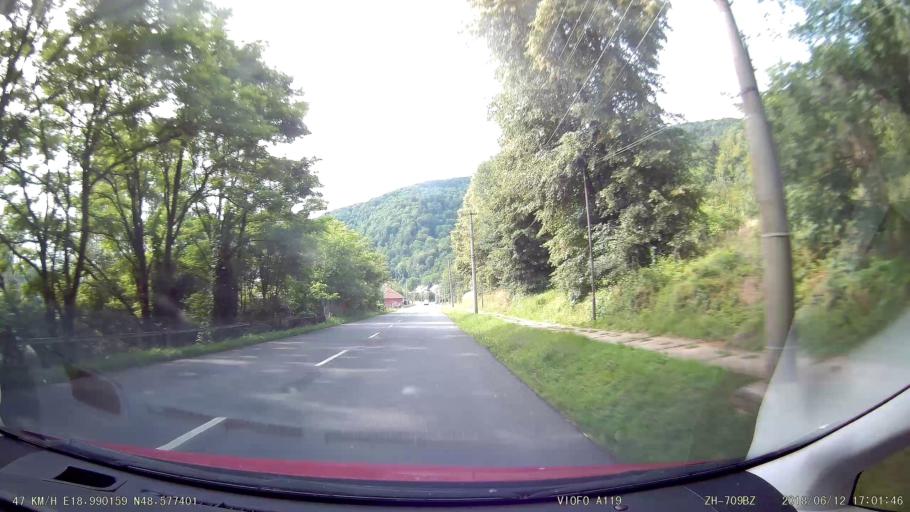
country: SK
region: Banskobystricky
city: Ziar nad Hronom
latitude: 48.5775
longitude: 18.9900
